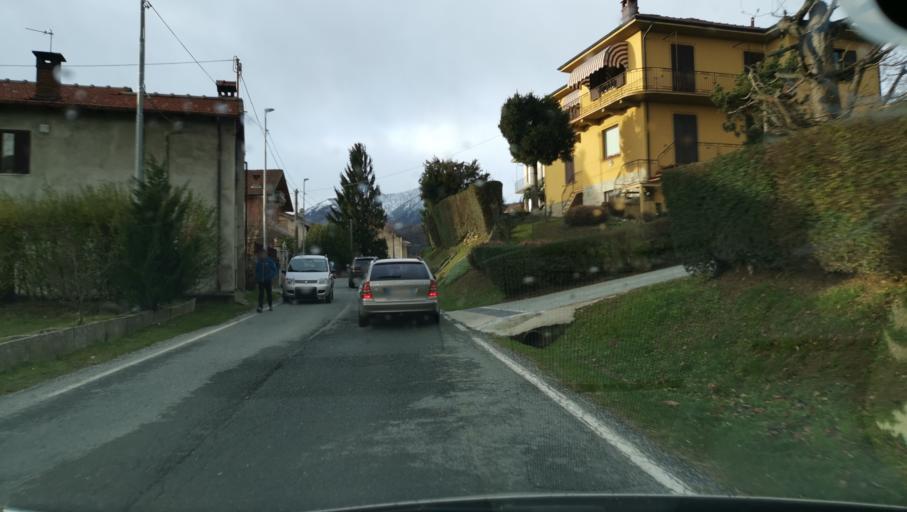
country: IT
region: Piedmont
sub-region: Provincia di Torino
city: Coazze
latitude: 45.0539
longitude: 7.3079
